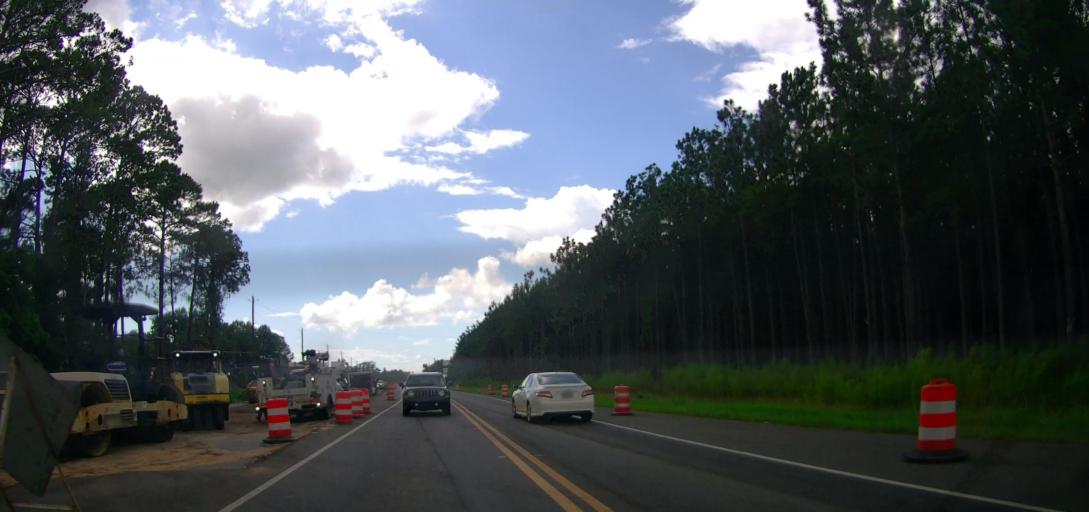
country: US
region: Georgia
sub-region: Coffee County
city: Douglas
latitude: 31.5197
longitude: -82.8887
